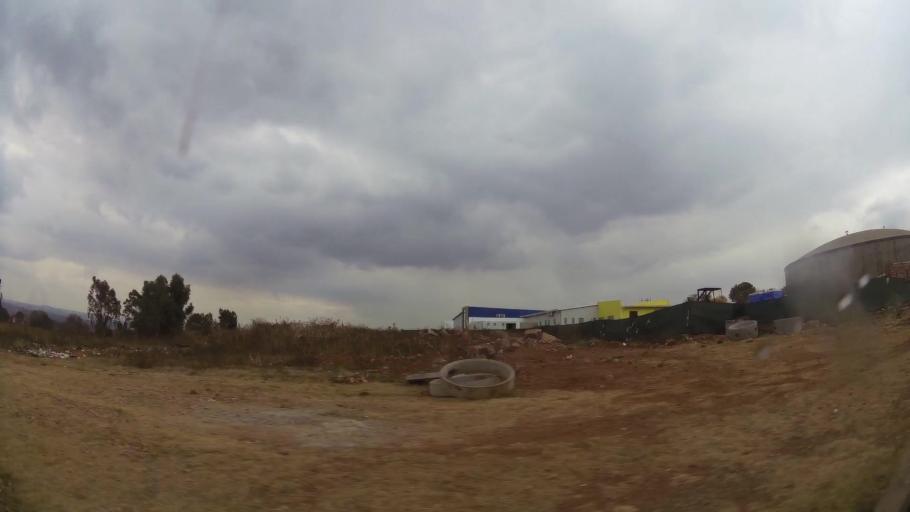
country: ZA
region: Gauteng
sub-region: Ekurhuleni Metropolitan Municipality
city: Germiston
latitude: -26.3787
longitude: 28.1271
